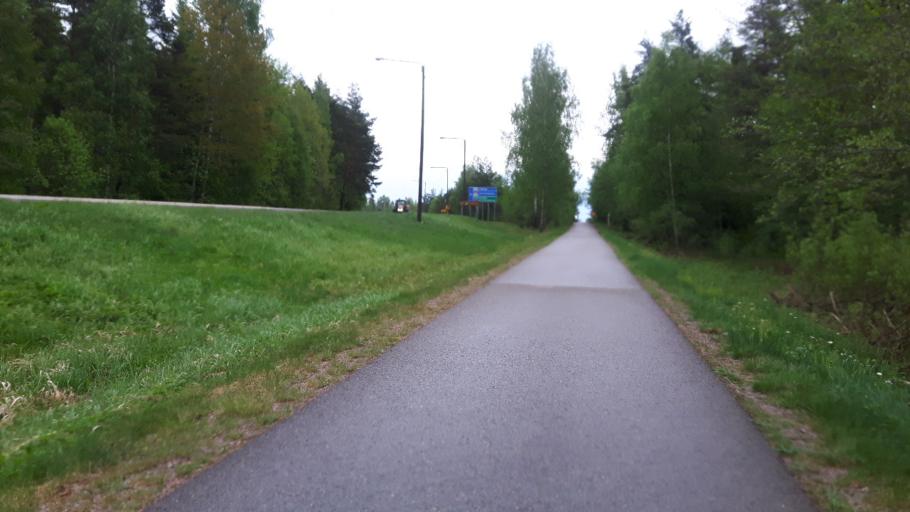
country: FI
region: Kymenlaakso
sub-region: Kotka-Hamina
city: Hamina
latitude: 60.5651
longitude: 27.1140
